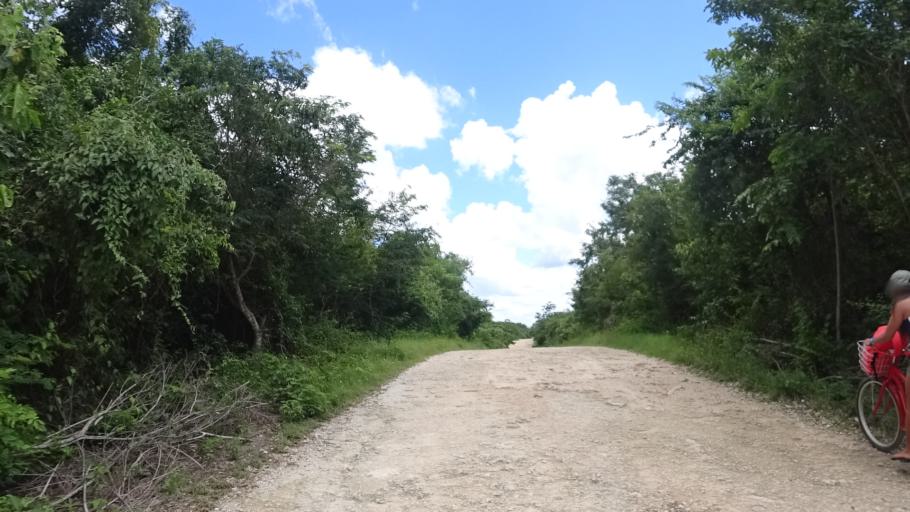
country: MX
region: Yucatan
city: Valladolid
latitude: 20.6733
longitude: -88.2255
